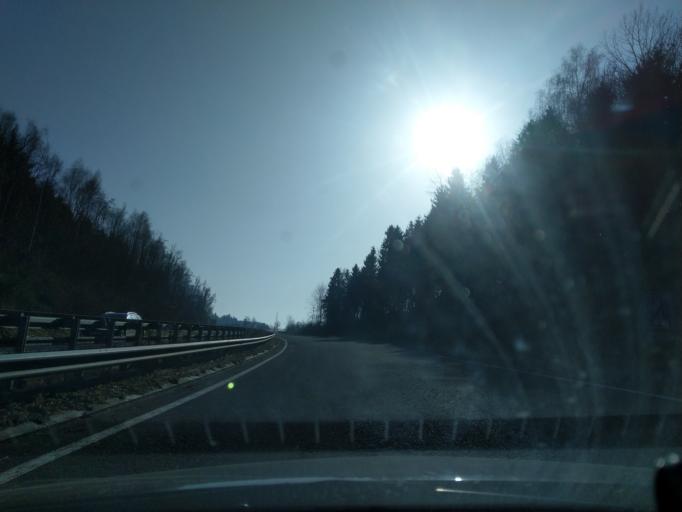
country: AT
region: Upper Austria
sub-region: Politischer Bezirk Ried im Innkreis
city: Ried im Innkreis
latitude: 48.2456
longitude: 13.5145
